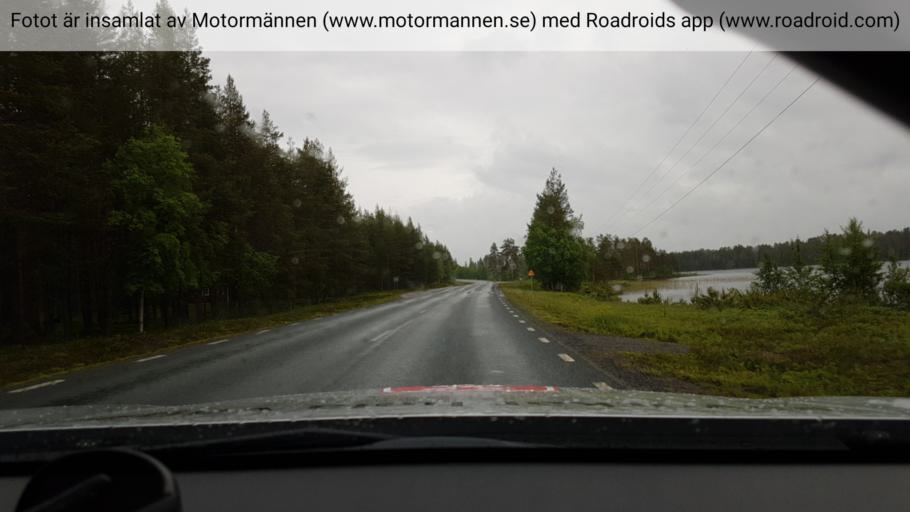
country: SE
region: Vaesterbotten
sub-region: Mala Kommun
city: Mala
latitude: 65.2280
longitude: 18.6232
